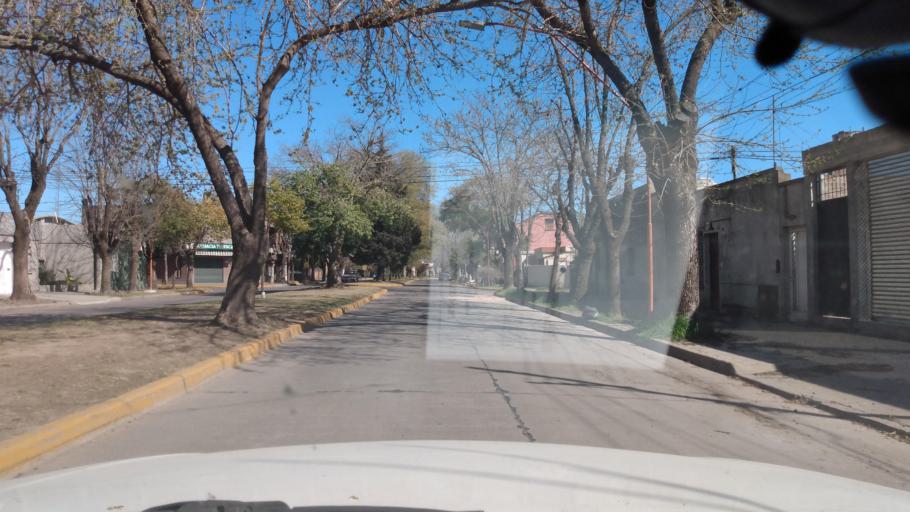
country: AR
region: Buenos Aires
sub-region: Partido de Mercedes
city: Mercedes
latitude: -34.6508
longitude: -59.4177
